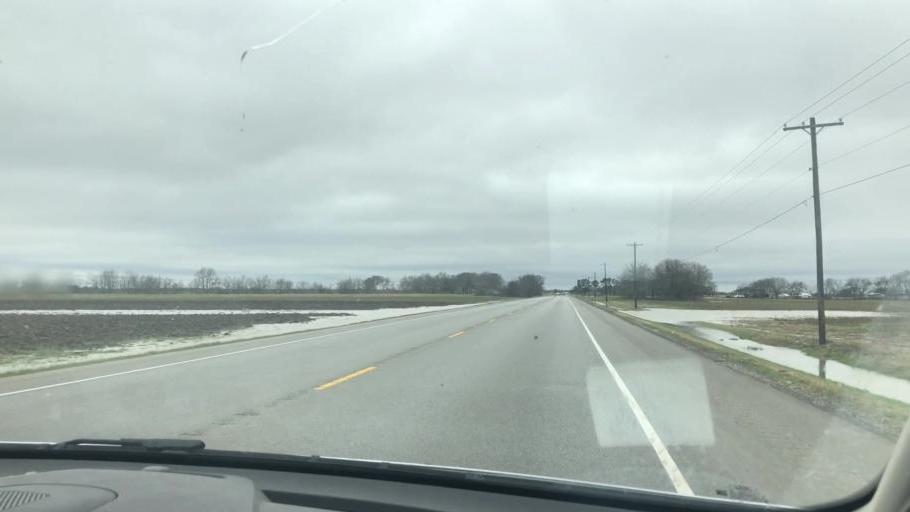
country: US
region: Texas
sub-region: Matagorda County
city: Bay City
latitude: 29.0482
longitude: -95.9714
